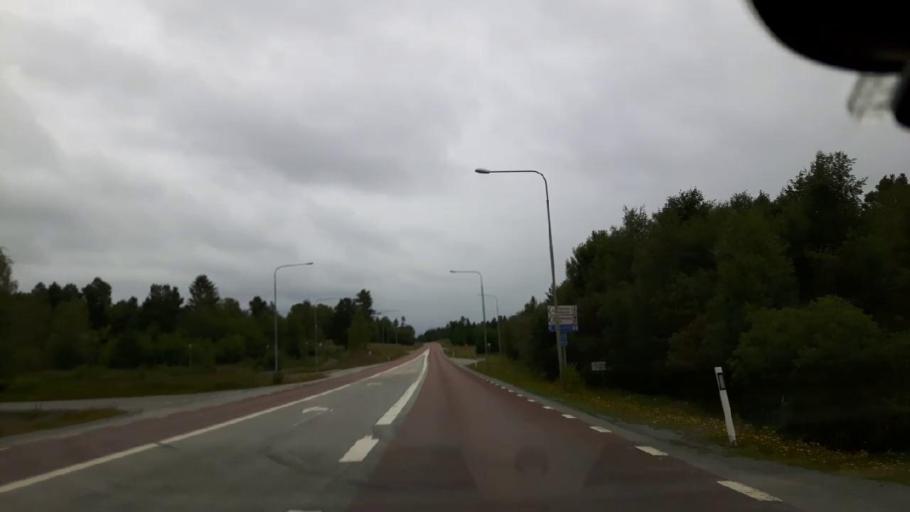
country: SE
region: Jaemtland
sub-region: Bergs Kommun
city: Hoverberg
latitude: 62.9153
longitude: 14.5278
